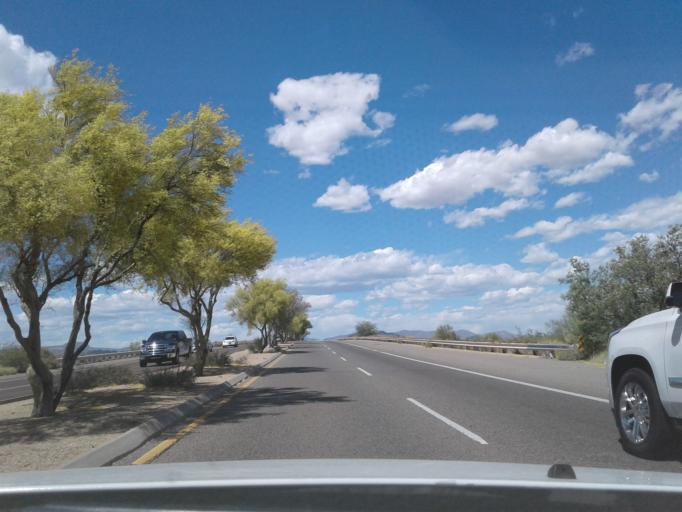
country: US
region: Arizona
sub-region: Maricopa County
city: Cave Creek
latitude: 33.7178
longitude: -112.0138
